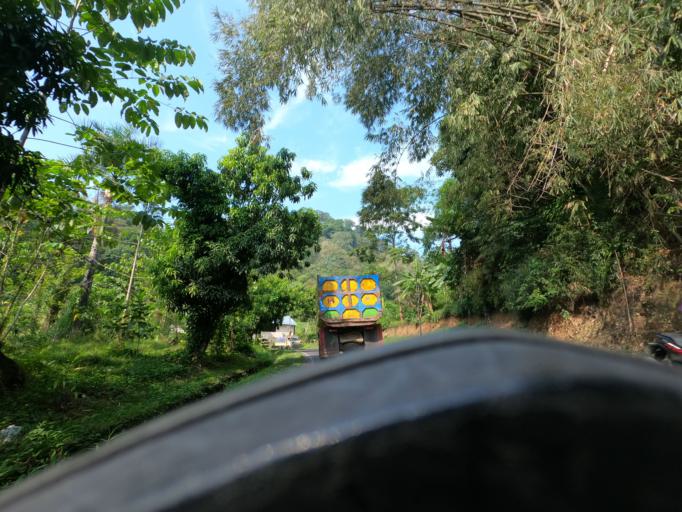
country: ID
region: West Java
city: Lembang
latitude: -6.6366
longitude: 107.7235
